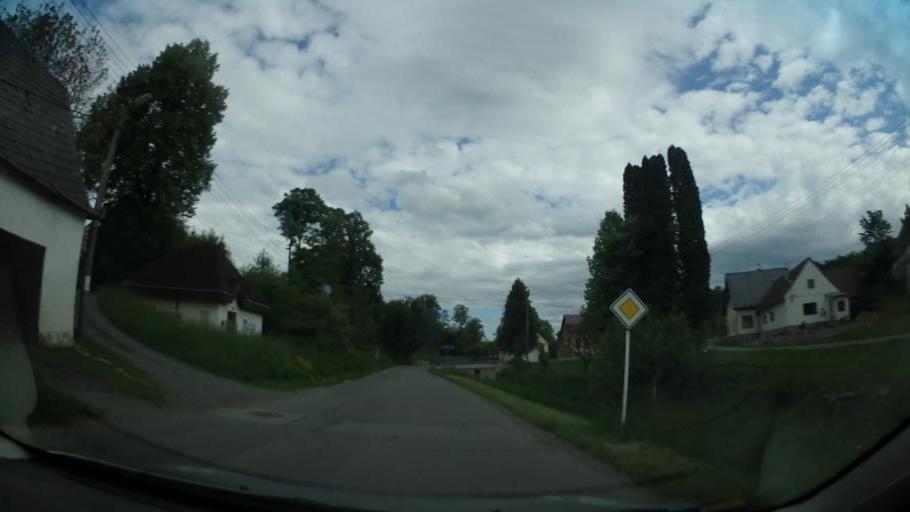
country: CZ
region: Pardubicky
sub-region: Okres Svitavy
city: Moravska Trebova
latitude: 49.8286
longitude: 16.7022
